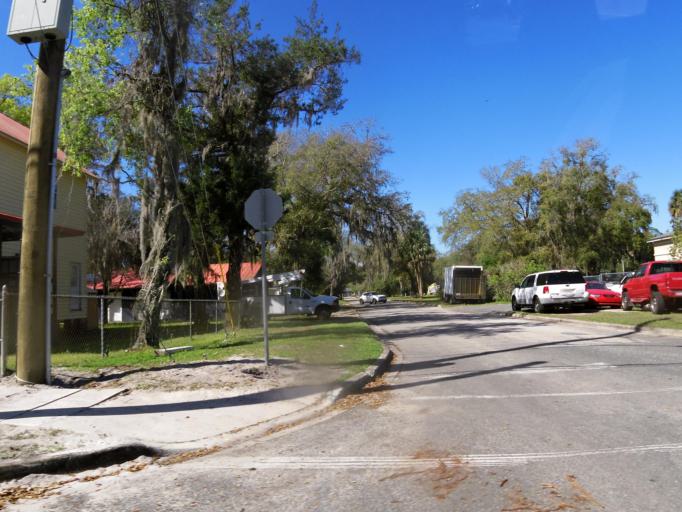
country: US
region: Florida
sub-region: Clay County
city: Green Cove Springs
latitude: 29.9960
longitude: -81.6814
